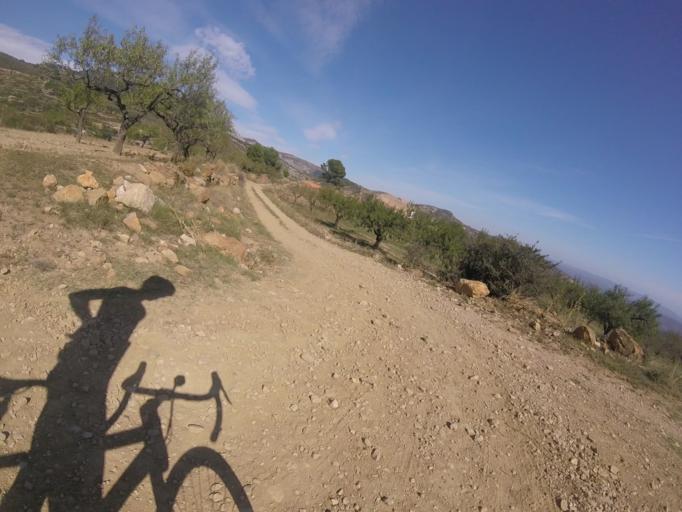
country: ES
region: Valencia
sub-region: Provincia de Castello
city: Sierra-Engarceran
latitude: 40.2736
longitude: 0.0035
